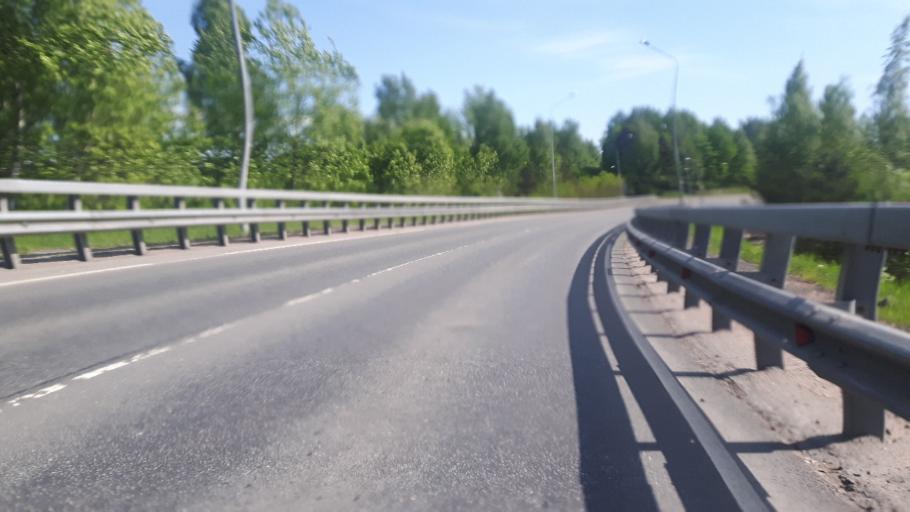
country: RU
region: Leningrad
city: Vyborg
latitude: 60.7352
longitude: 28.6974
